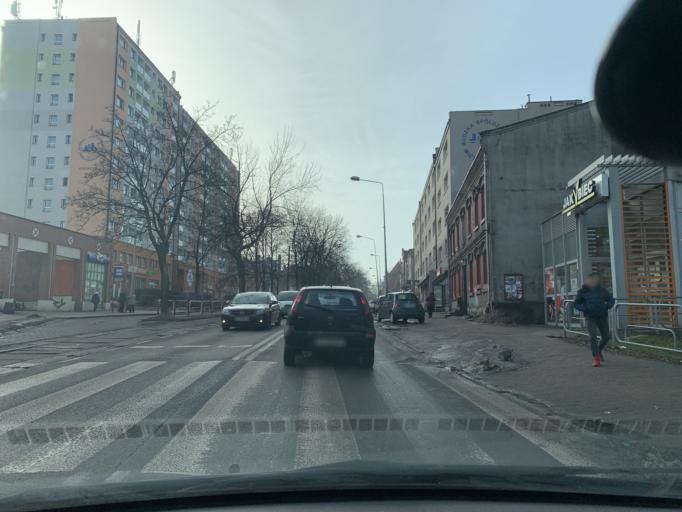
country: PL
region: Silesian Voivodeship
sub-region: Ruda Slaska
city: Ruda Slaska
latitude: 50.3127
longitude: 18.8518
